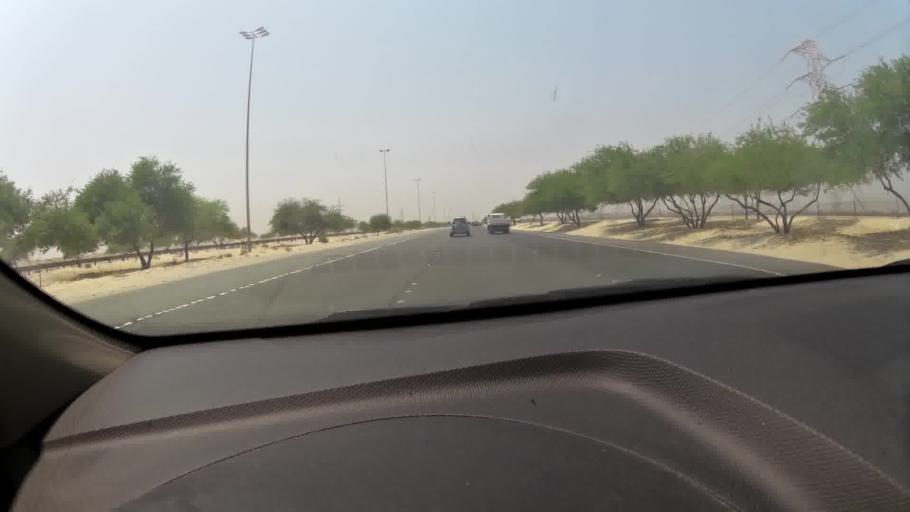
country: KW
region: Al Ahmadi
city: Al Fahahil
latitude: 28.9352
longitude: 48.1644
